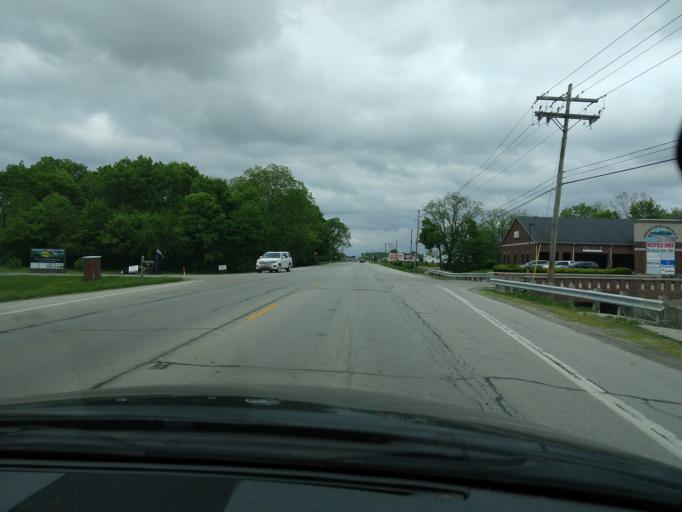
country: US
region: Indiana
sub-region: Hamilton County
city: Westfield
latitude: 40.0428
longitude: -86.1176
